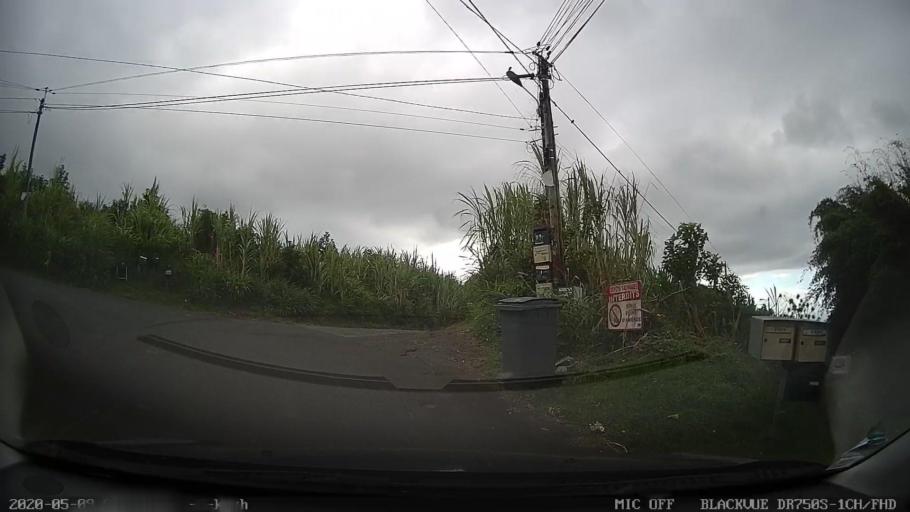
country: RE
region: Reunion
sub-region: Reunion
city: Sainte-Marie
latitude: -20.9457
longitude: 55.5255
